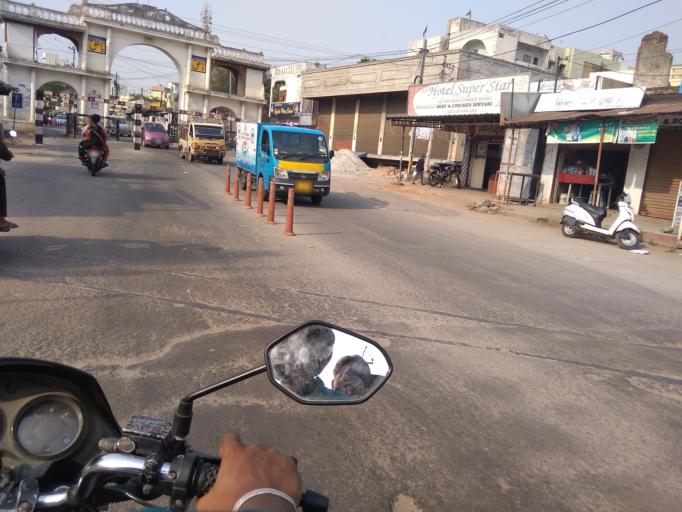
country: IN
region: Telangana
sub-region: Hyderabad
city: Malkajgiri
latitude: 17.4607
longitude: 78.5580
